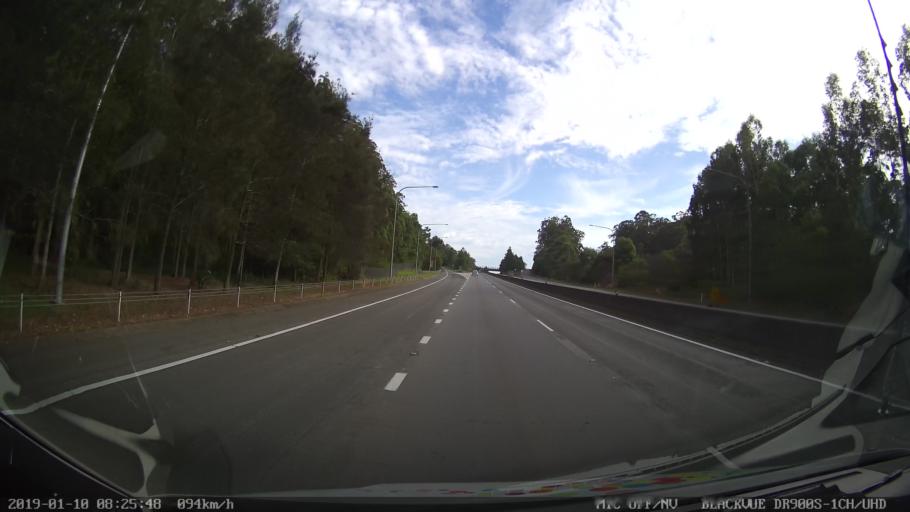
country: AU
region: New South Wales
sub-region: Coffs Harbour
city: Bonville
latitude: -30.4290
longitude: 153.0194
